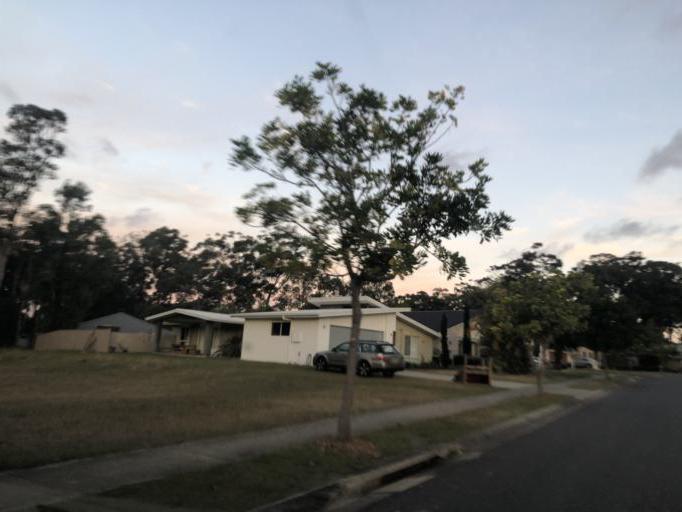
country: AU
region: New South Wales
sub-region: Coffs Harbour
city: Woolgoolga
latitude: -30.0932
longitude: 153.1923
